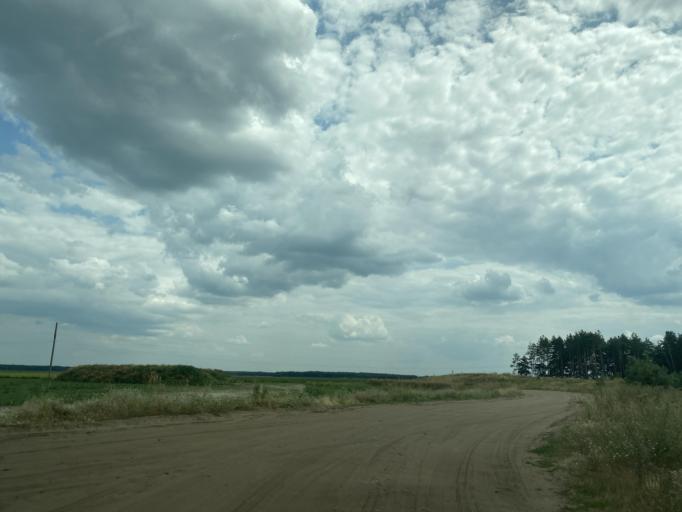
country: BY
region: Brest
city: Ivanava
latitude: 52.3655
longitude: 25.6366
